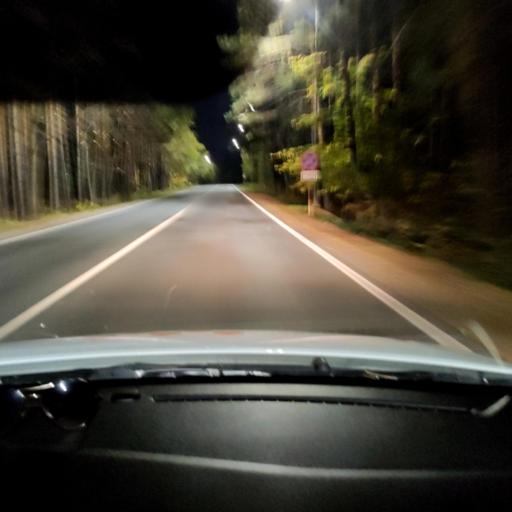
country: RU
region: Tatarstan
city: Verkhniy Uslon
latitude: 55.6350
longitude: 49.0198
